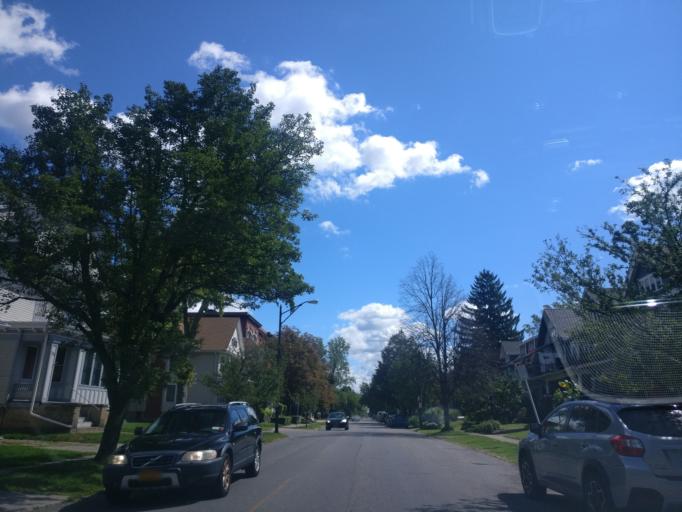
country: US
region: New York
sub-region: Erie County
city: Buffalo
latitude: 42.9222
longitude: -78.8745
